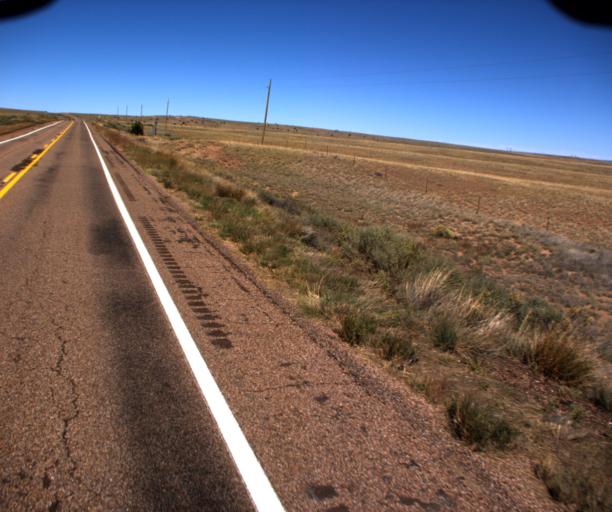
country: US
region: Arizona
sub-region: Apache County
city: Saint Johns
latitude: 34.5177
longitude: -109.4514
